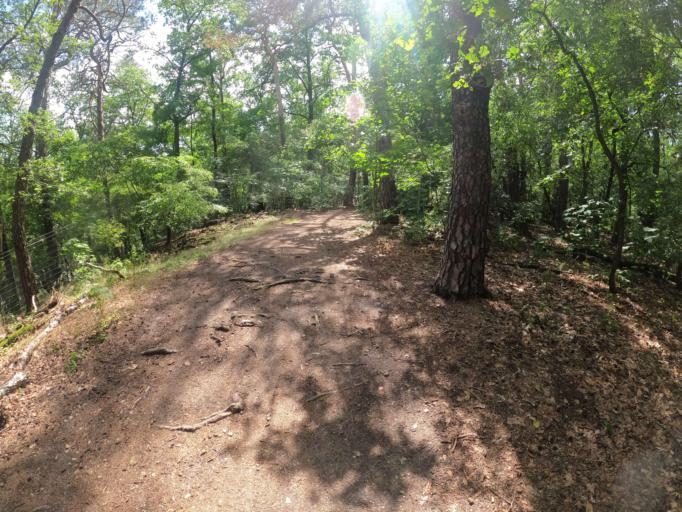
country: DE
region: Berlin
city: Haselhorst
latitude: 52.5171
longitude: 13.2290
